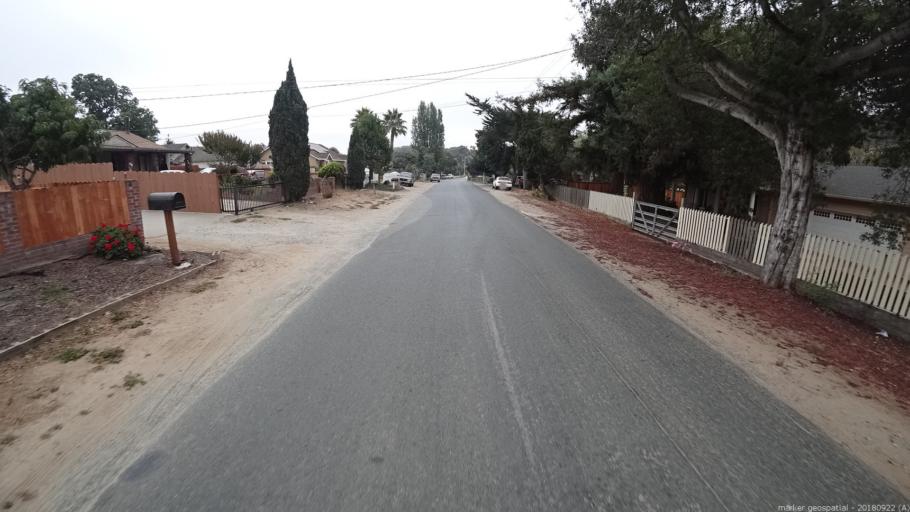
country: US
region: California
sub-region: Monterey County
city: Prunedale
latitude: 36.7761
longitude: -121.6717
